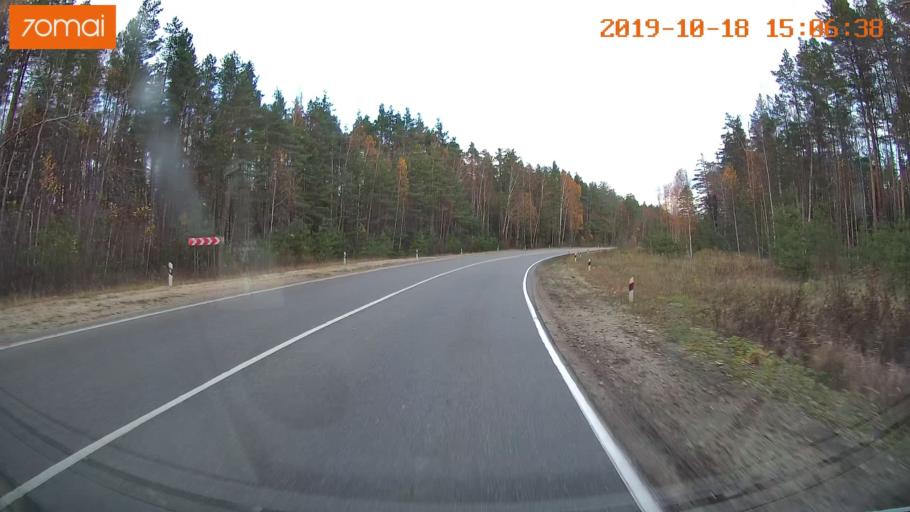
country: RU
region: Vladimir
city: Gus'-Khrustal'nyy
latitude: 55.5328
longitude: 40.5801
